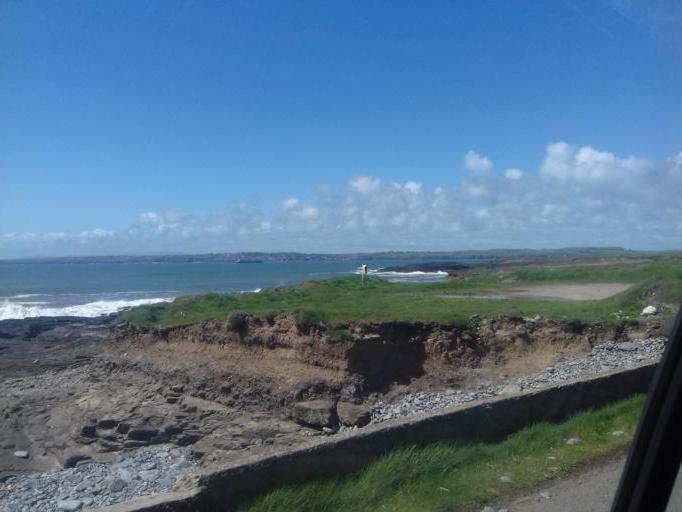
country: IE
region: Munster
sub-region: Waterford
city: Dunmore East
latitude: 52.1276
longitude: -6.9293
